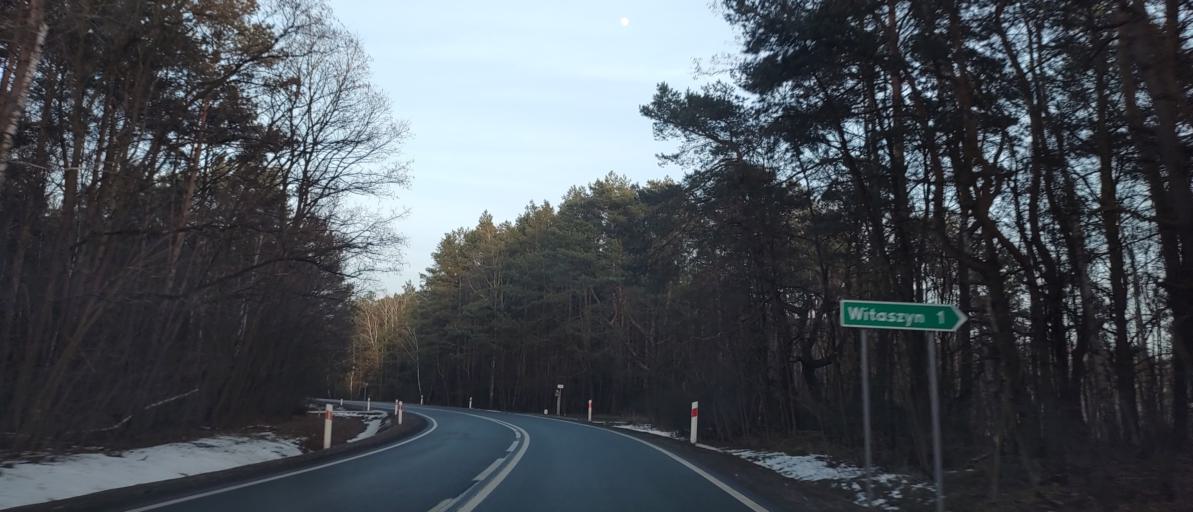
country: PL
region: Masovian Voivodeship
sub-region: Powiat bialobrzeski
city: Sucha
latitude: 51.6290
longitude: 20.8847
